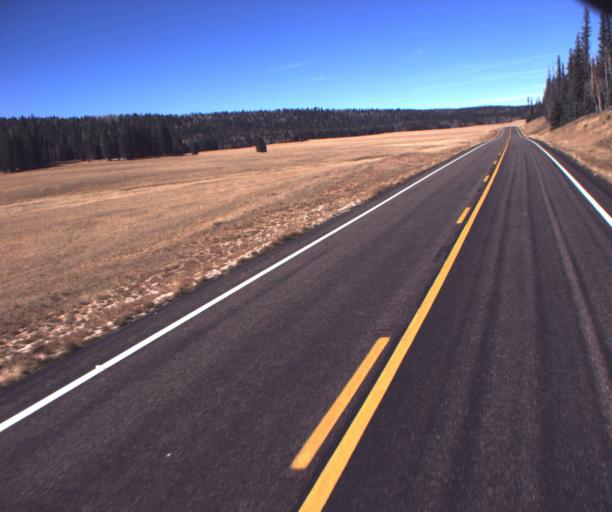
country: US
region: Arizona
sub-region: Coconino County
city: Grand Canyon
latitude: 36.3718
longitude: -112.1232
